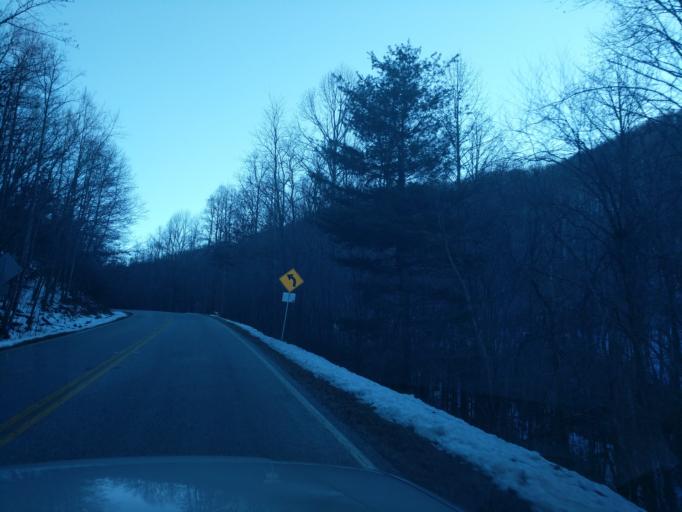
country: US
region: Georgia
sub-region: Towns County
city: Hiawassee
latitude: 34.9177
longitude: -83.6245
